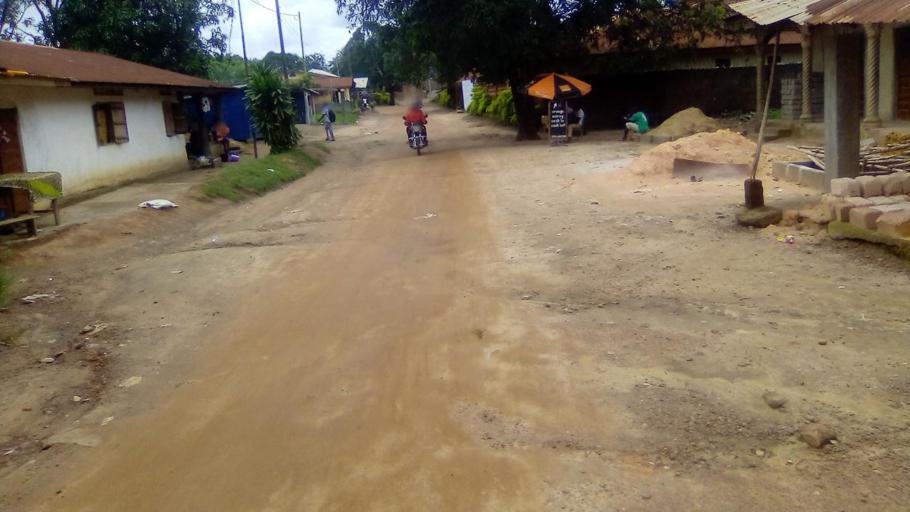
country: SL
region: Southern Province
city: Bo
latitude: 7.9431
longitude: -11.7406
